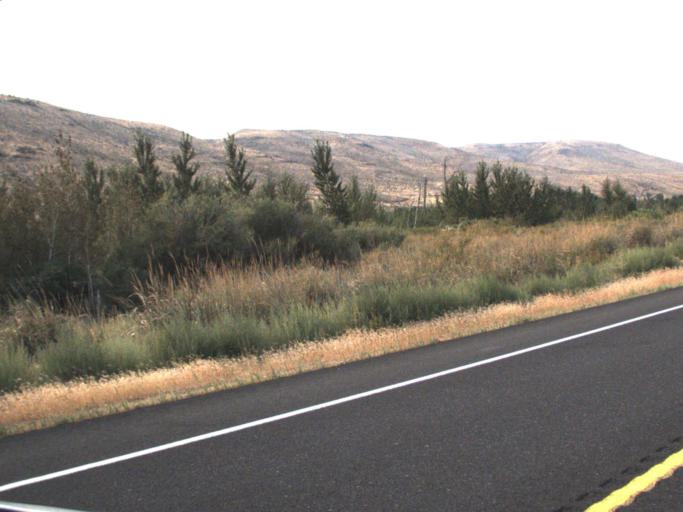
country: US
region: Washington
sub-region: Yakima County
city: Toppenish
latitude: 46.1910
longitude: -120.4917
